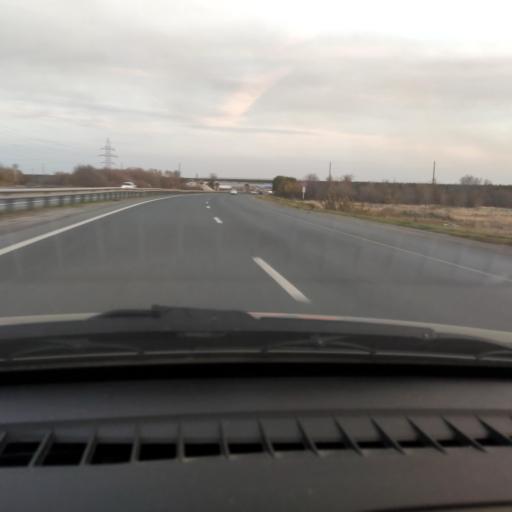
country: RU
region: Samara
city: Tol'yatti
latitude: 53.5650
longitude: 49.4945
